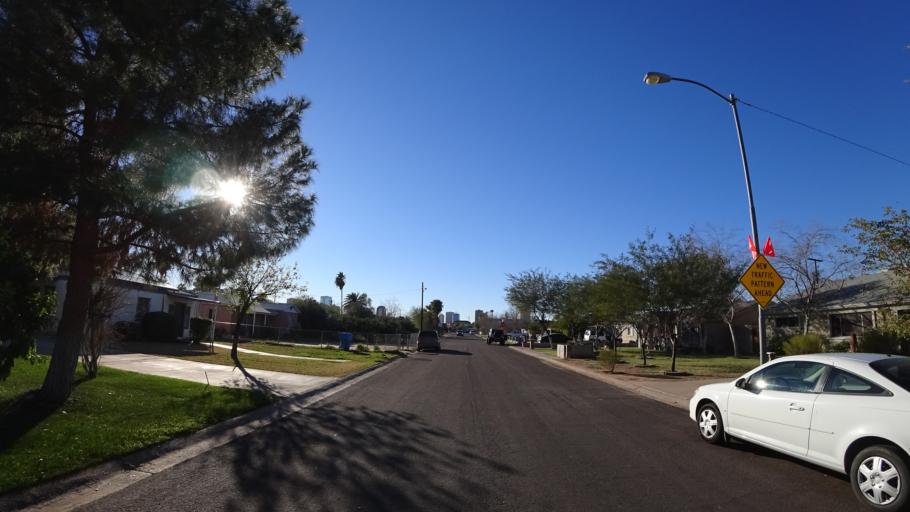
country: US
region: Arizona
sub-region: Maricopa County
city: Phoenix
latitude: 33.4920
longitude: -112.0590
